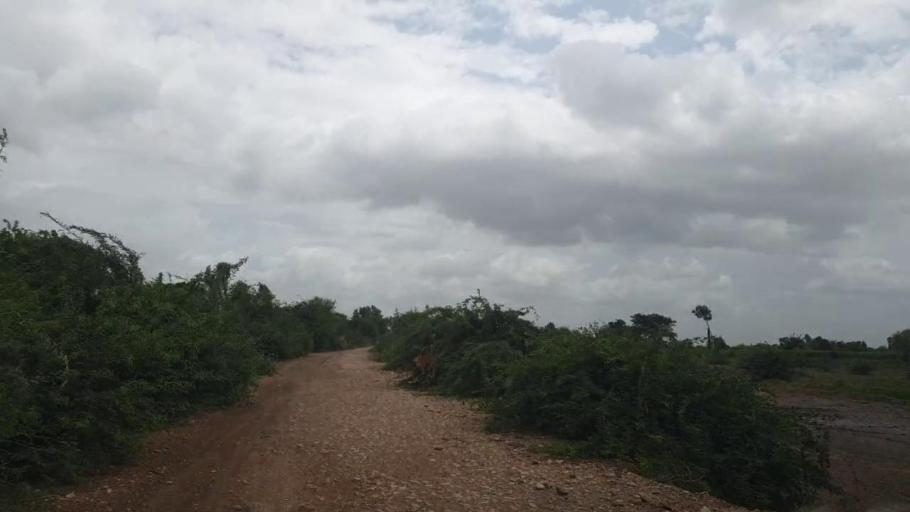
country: PK
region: Sindh
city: Badin
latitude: 24.6360
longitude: 68.9487
